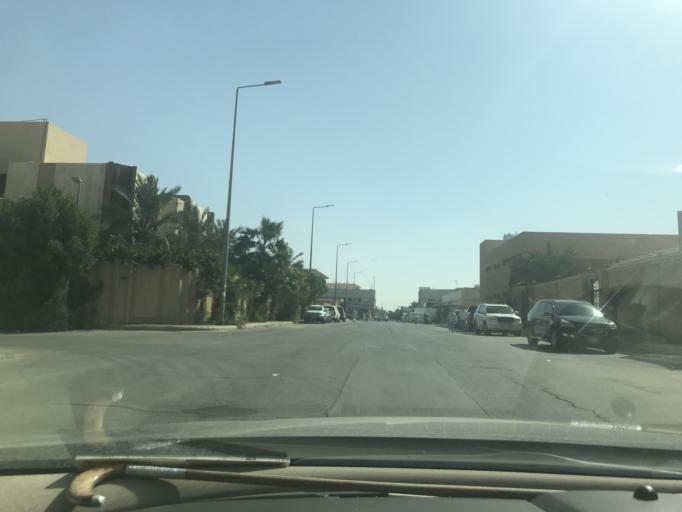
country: SA
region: Ar Riyad
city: Riyadh
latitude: 24.7332
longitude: 46.7654
